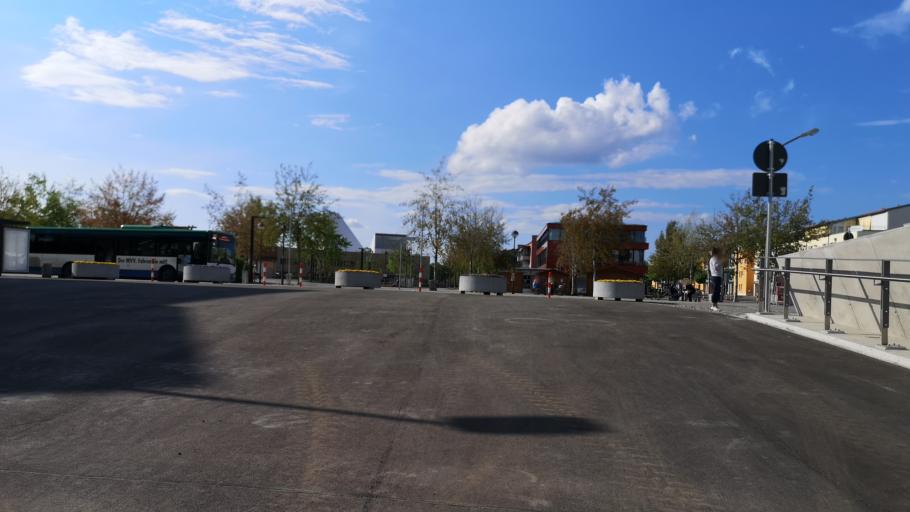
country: DE
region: Bavaria
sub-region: Upper Bavaria
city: Poing
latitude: 48.1715
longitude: 11.8094
